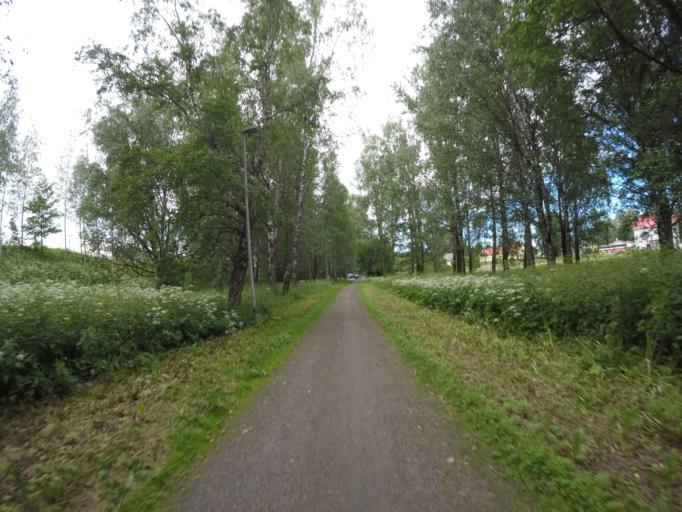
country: FI
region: Haeme
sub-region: Haemeenlinna
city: Haemeenlinna
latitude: 61.0057
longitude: 24.4381
